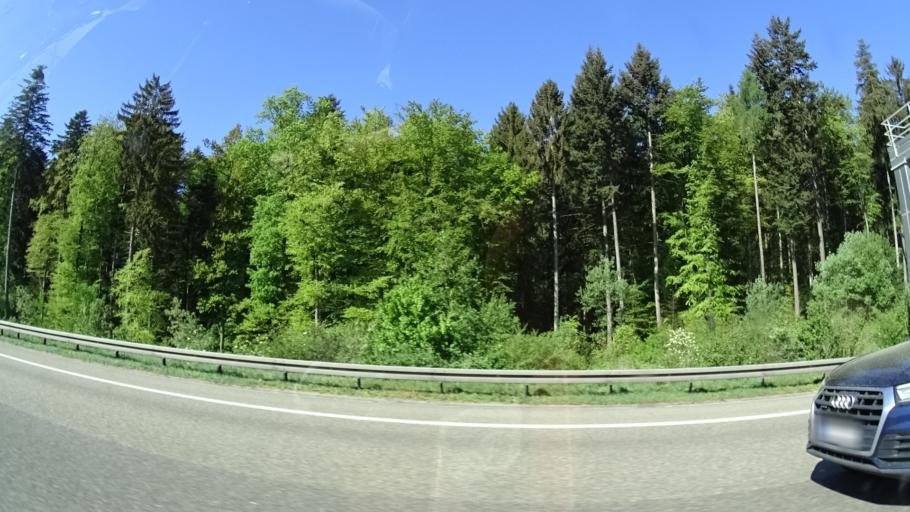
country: DE
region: Baden-Wuerttemberg
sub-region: Karlsruhe Region
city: Niefern-Oschelbronn
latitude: 48.8916
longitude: 8.7862
